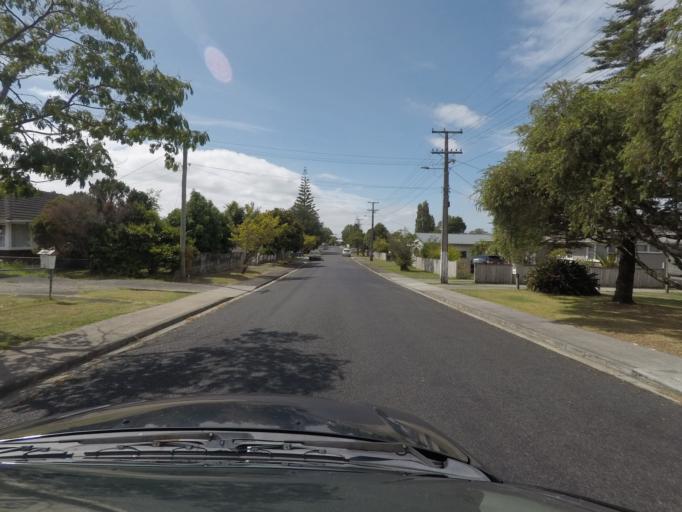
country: NZ
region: Auckland
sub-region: Auckland
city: Rosebank
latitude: -36.8928
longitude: 174.6673
